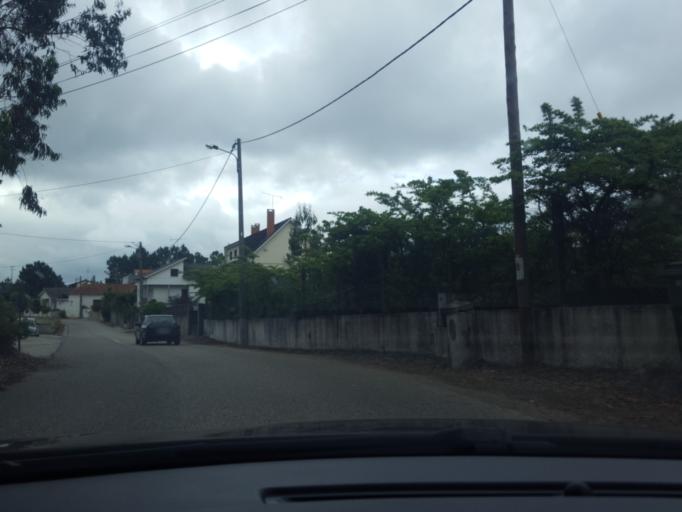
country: PT
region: Leiria
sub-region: Leiria
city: Caranguejeira
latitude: 39.7908
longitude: -8.7487
